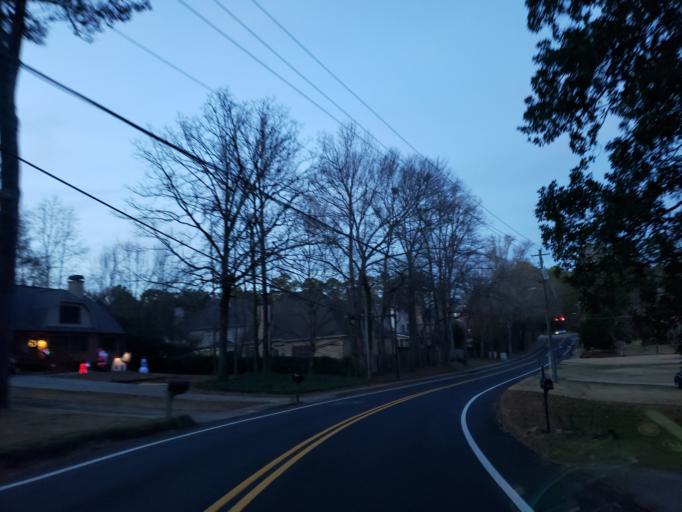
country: US
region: Georgia
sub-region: DeKalb County
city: North Druid Hills
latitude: 33.8271
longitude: -84.2800
